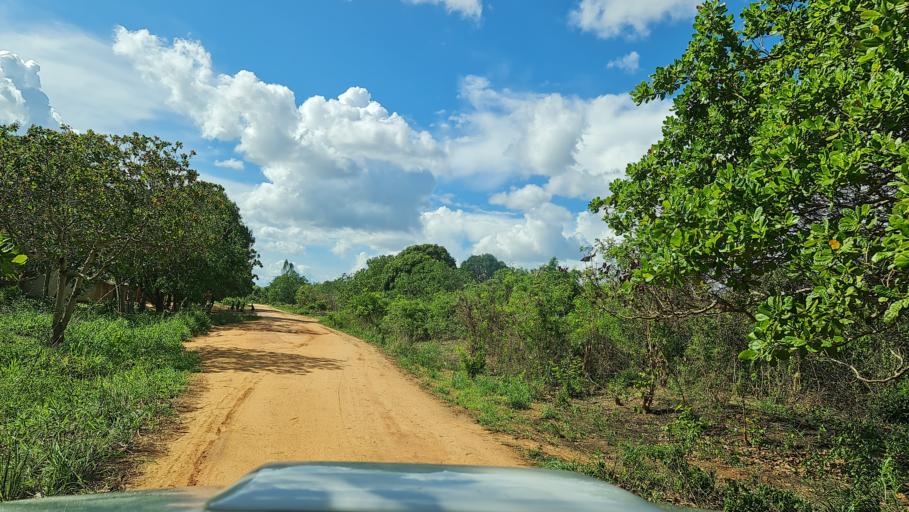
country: MZ
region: Nampula
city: Ilha de Mocambique
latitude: -15.4285
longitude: 40.2722
